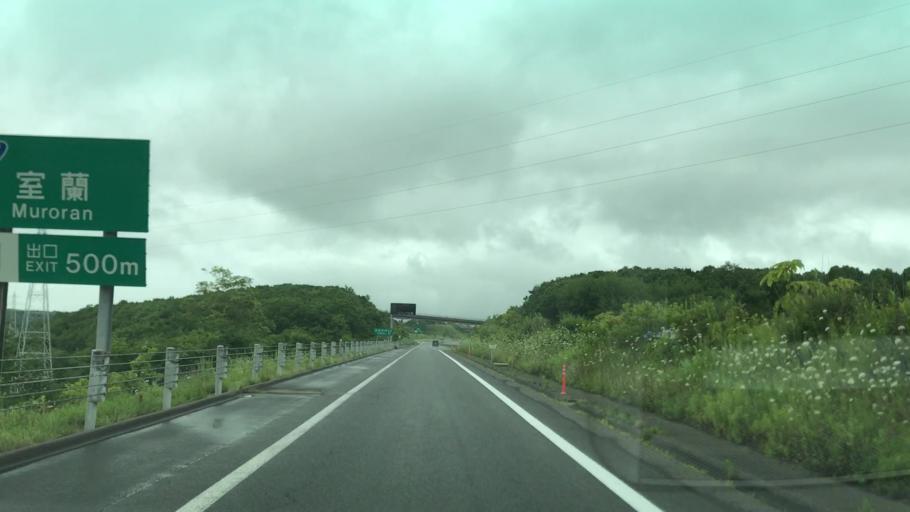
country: JP
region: Hokkaido
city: Muroran
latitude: 42.3857
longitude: 140.9805
